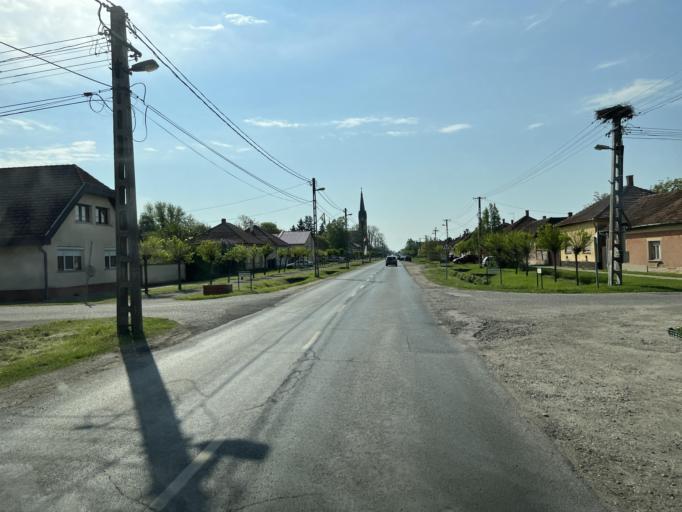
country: HU
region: Pest
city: Jaszkarajeno
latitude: 47.0566
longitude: 20.0628
